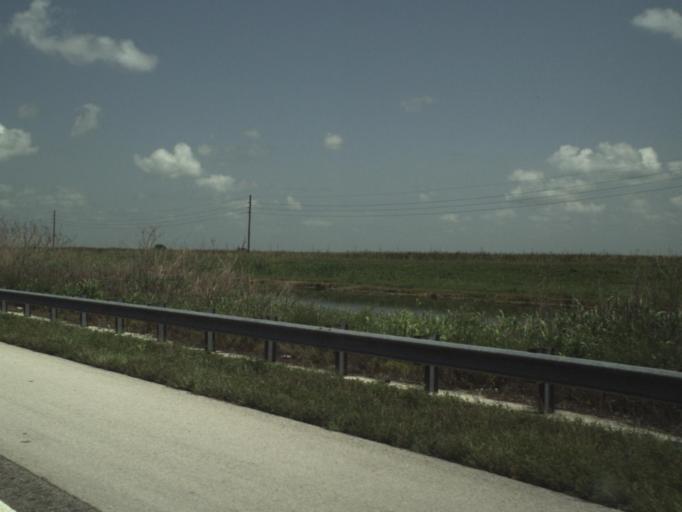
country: US
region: Florida
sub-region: Broward County
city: Coral Springs
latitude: 26.3658
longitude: -80.5615
